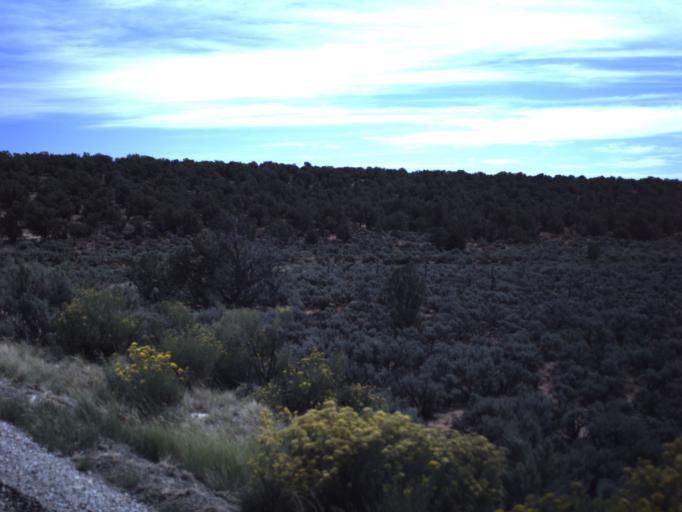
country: US
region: Utah
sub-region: San Juan County
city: Blanding
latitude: 37.5759
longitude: -109.5327
